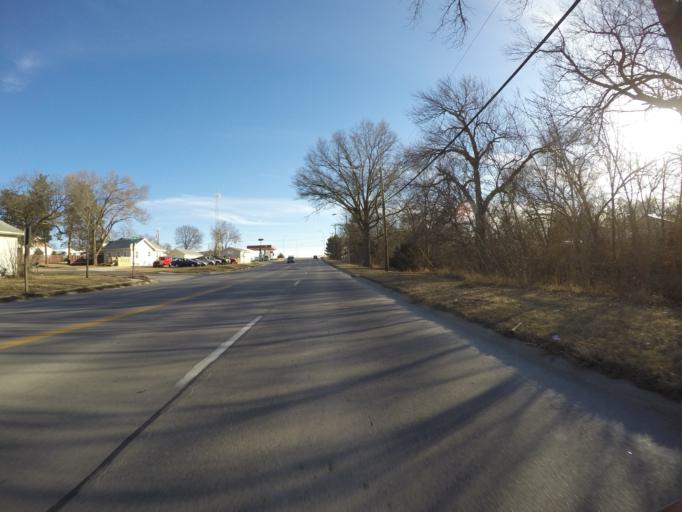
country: US
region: Nebraska
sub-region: Gage County
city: Beatrice
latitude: 40.2495
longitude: -96.7459
